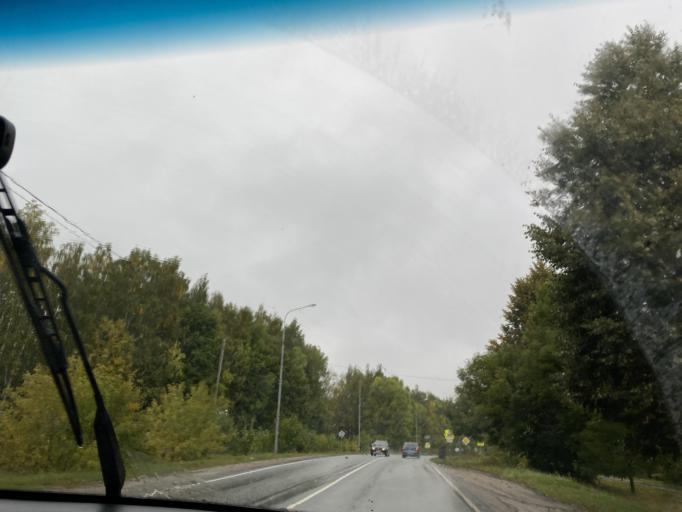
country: RU
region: Rjazan
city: Starozhilovo
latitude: 54.4445
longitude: 39.8901
